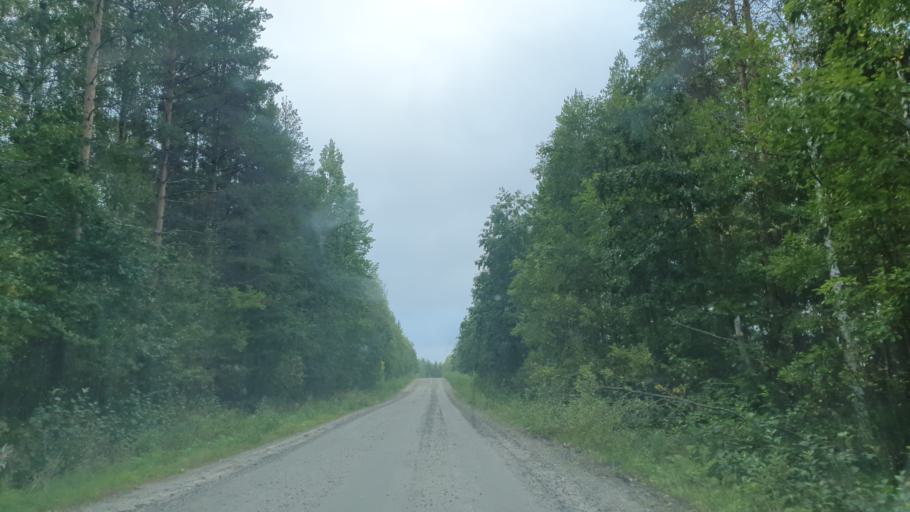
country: FI
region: Kainuu
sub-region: Kehys-Kainuu
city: Kuhmo
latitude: 64.1378
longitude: 29.5945
